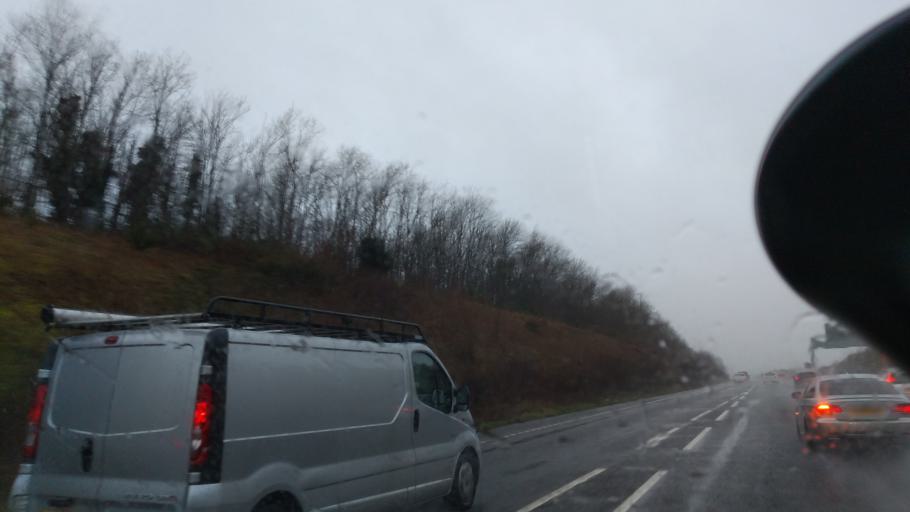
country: GB
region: England
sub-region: West Sussex
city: Shoreham-by-Sea
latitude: 50.8453
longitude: -0.2596
